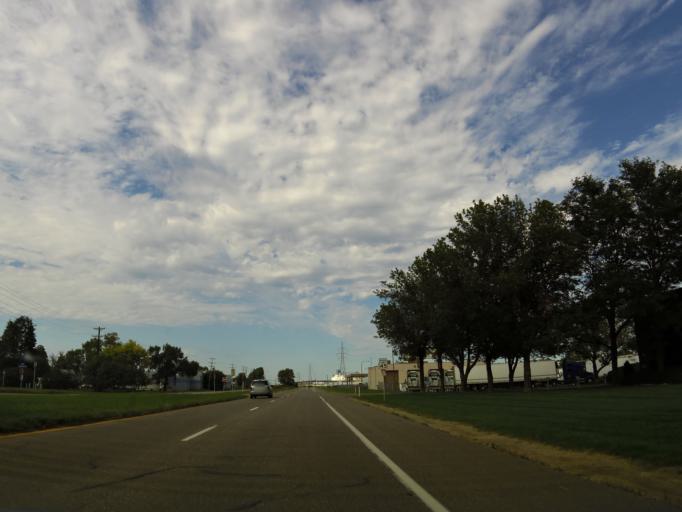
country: US
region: Minnesota
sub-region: Anoka County
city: Columbia Heights
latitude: 45.0317
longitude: -93.2765
